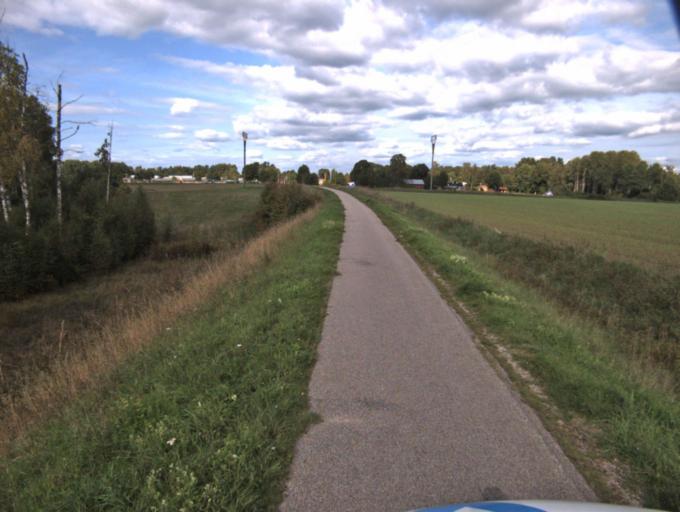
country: SE
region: Vaestra Goetaland
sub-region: Ulricehamns Kommun
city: Ulricehamn
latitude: 57.8524
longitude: 13.4271
